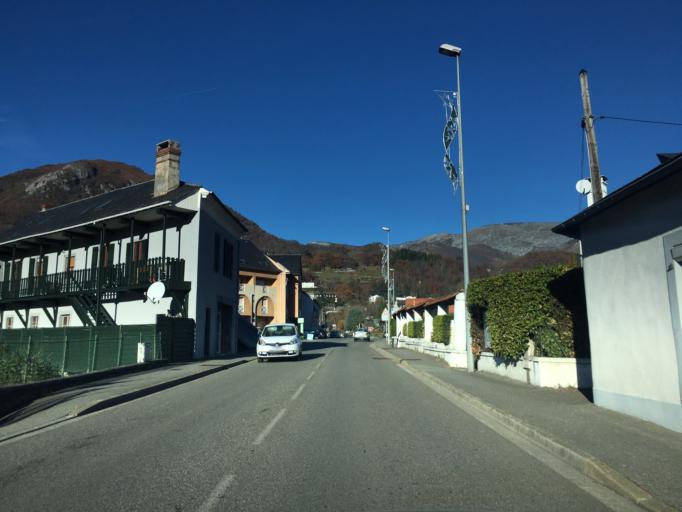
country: FR
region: Midi-Pyrenees
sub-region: Departement des Hautes-Pyrenees
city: Argeles-Gazost
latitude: 43.0006
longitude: -0.0980
